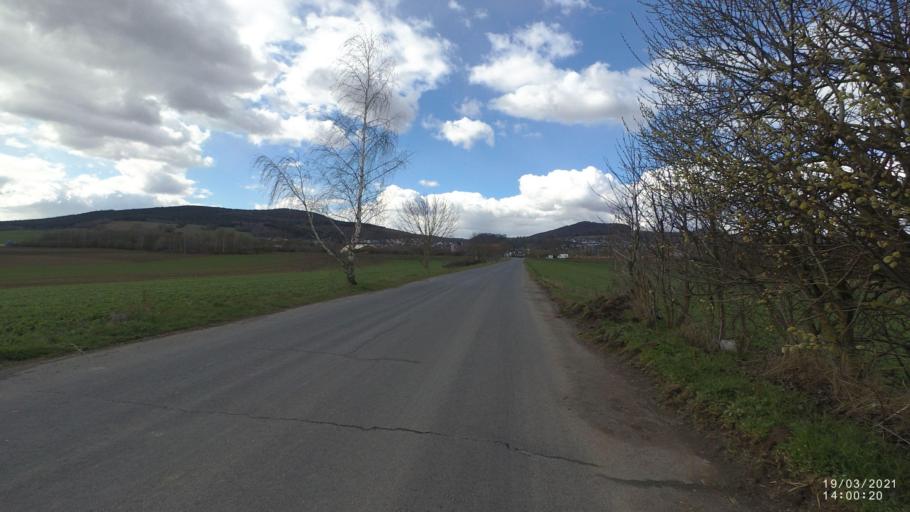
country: DE
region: Rheinland-Pfalz
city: Nickenich
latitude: 50.4064
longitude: 7.3405
